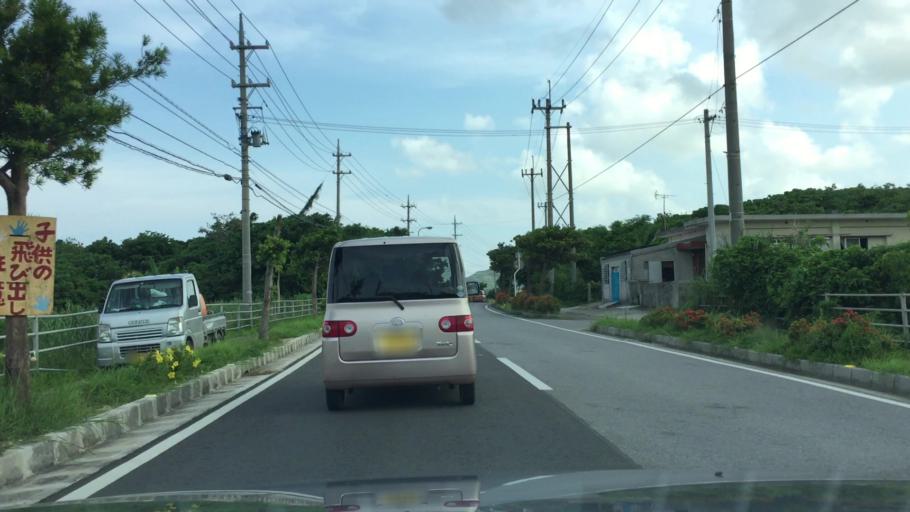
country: JP
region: Okinawa
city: Ishigaki
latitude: 24.4371
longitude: 124.2491
